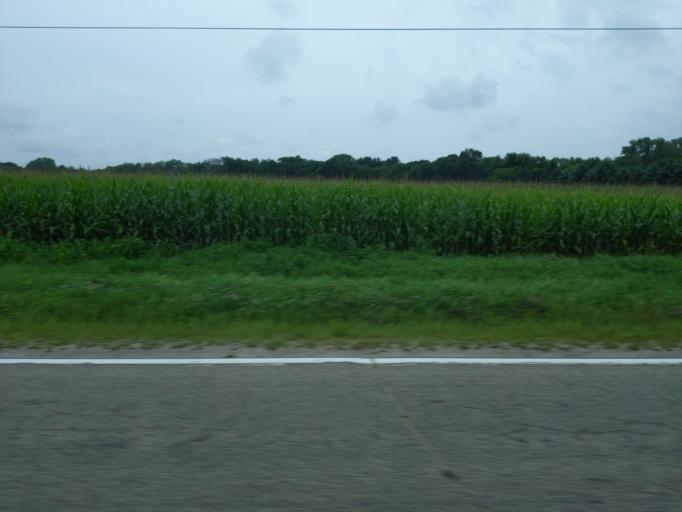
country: US
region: Wisconsin
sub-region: Sauk County
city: Sauk City
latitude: 43.2543
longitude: -89.7191
